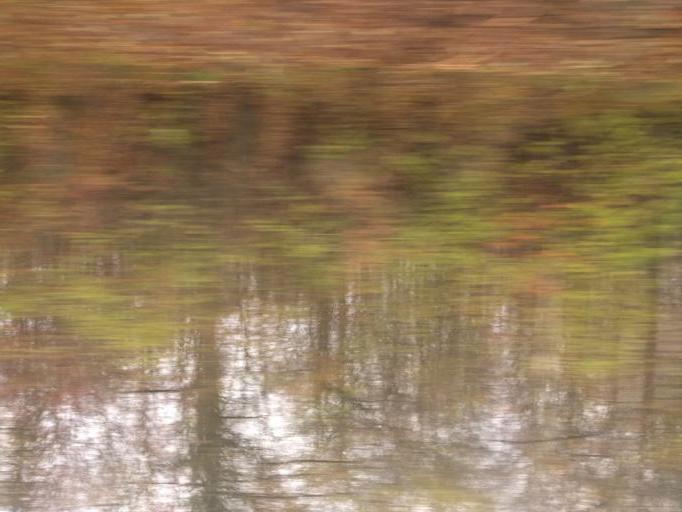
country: DK
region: Zealand
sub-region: Koge Kommune
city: Borup
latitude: 55.5150
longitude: 11.9761
